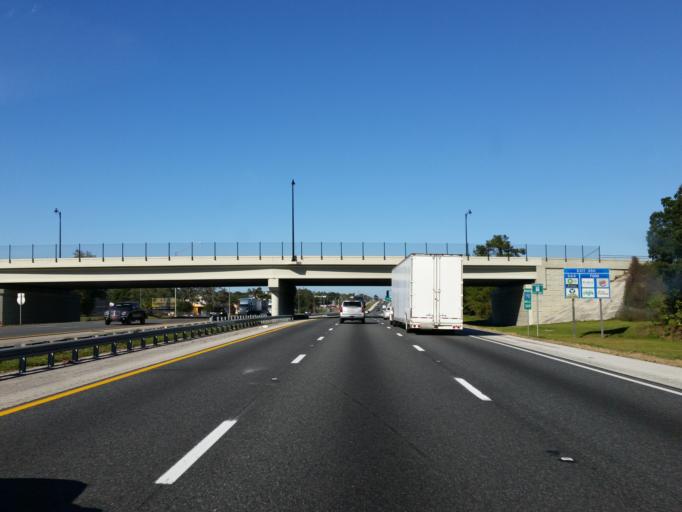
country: US
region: Florida
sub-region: Marion County
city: Ocala
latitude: 29.1415
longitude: -82.1849
